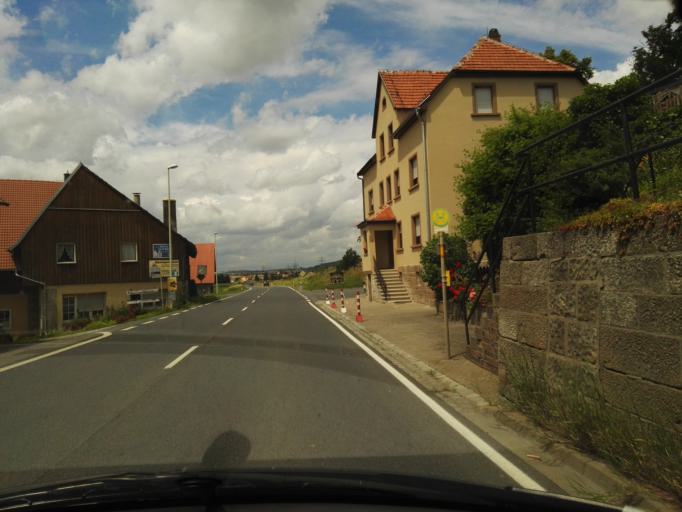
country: DE
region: Bavaria
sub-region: Upper Franconia
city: Redwitz an der Rodach
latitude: 50.1520
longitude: 11.2158
